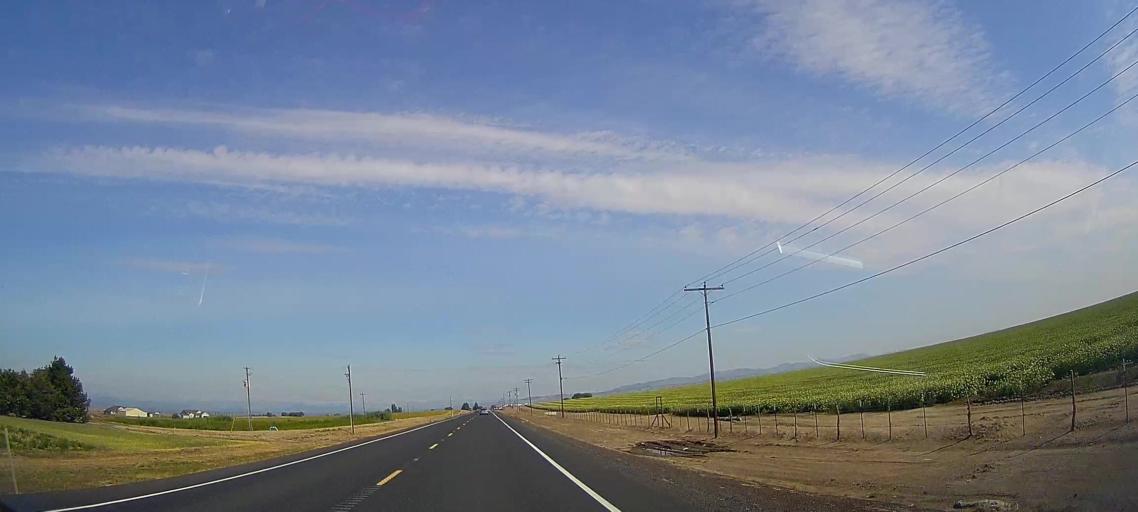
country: US
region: Oregon
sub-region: Jefferson County
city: Madras
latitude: 44.6814
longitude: -121.1480
